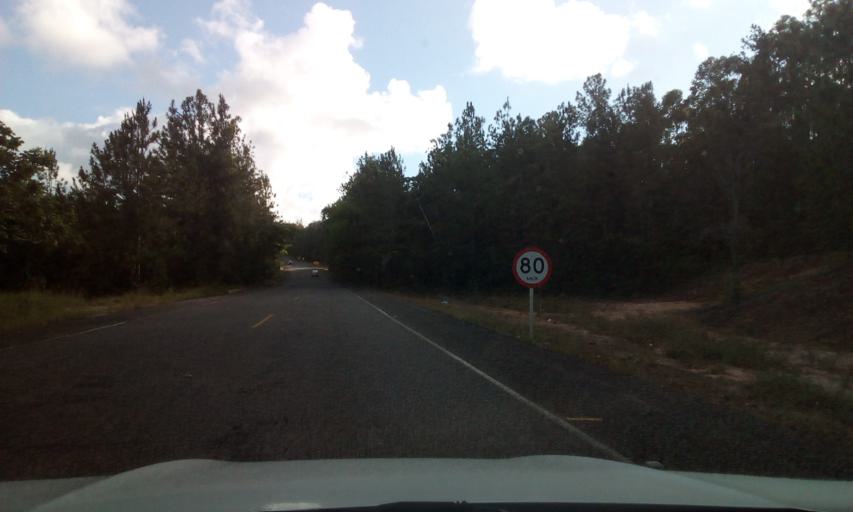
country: BR
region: Bahia
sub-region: Conde
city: Conde
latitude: -12.0997
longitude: -37.7778
